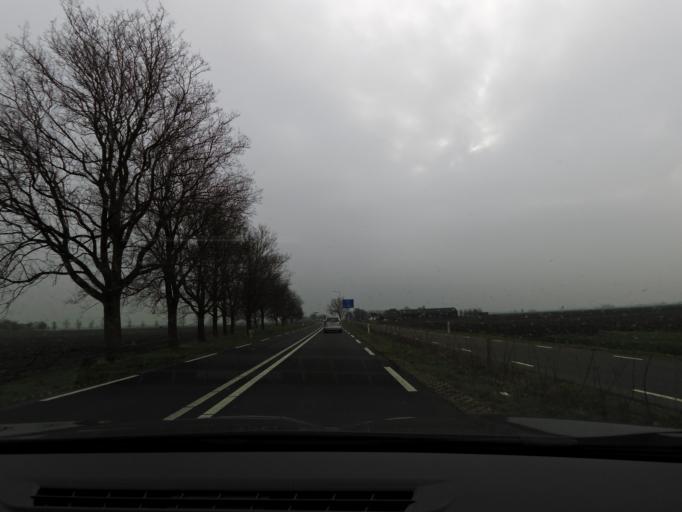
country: NL
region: South Holland
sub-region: Gemeente Nieuwkoop
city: Nieuwkoop
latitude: 52.1791
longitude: 4.7679
